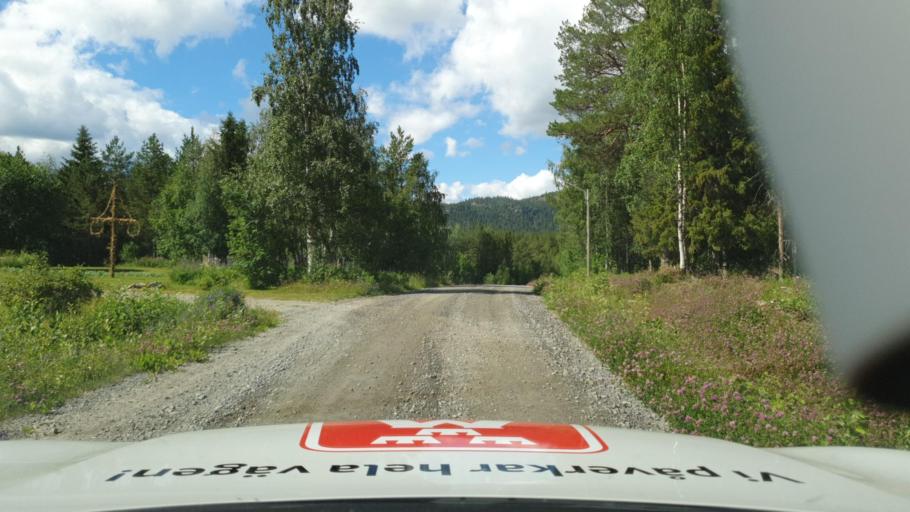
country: SE
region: Vaesterbotten
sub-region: Sorsele Kommun
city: Sorsele
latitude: 65.6408
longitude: 17.4214
